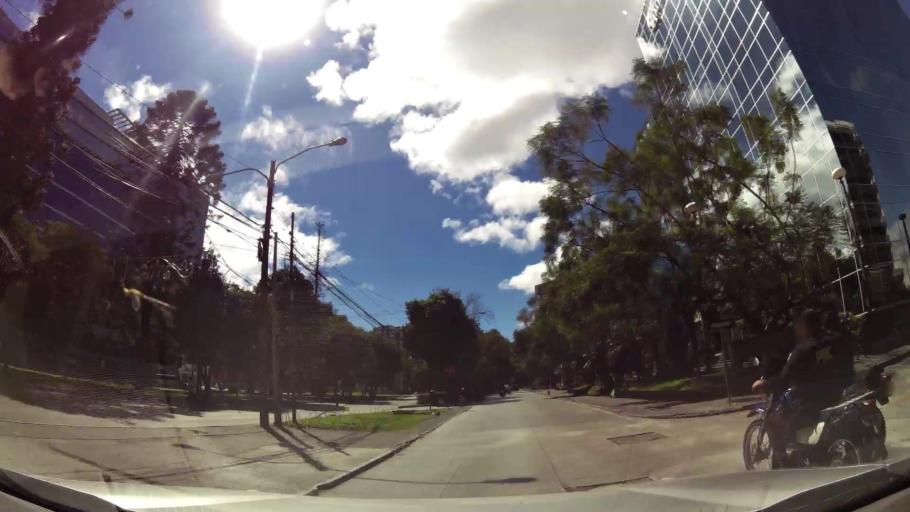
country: GT
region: Guatemala
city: Guatemala City
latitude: 14.6048
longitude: -90.5161
